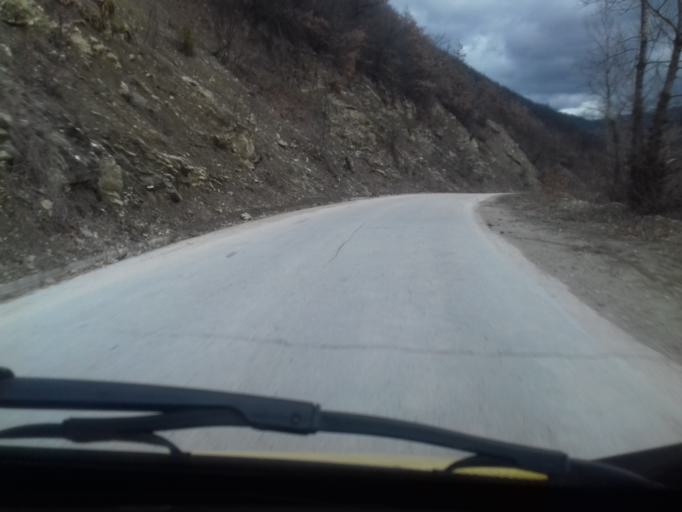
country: BA
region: Federation of Bosnia and Herzegovina
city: Zenica
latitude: 44.2246
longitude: 17.9702
